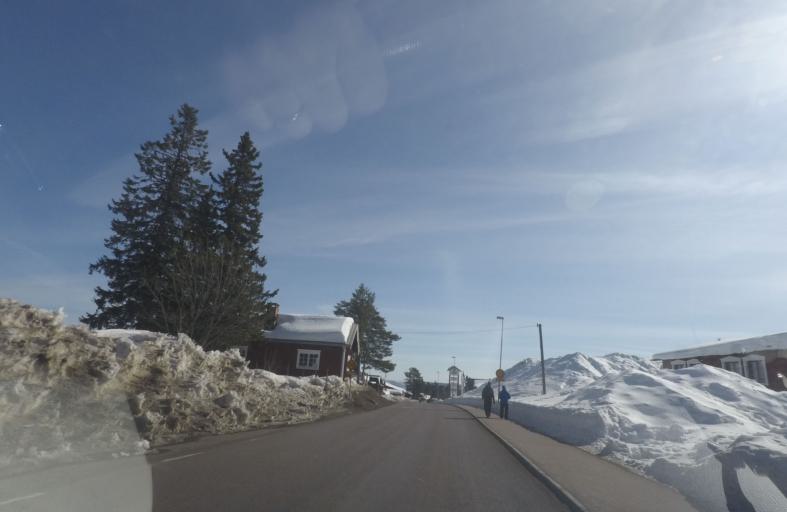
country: SE
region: Dalarna
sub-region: Malung-Saelens kommun
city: Malung
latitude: 61.1666
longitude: 13.1734
